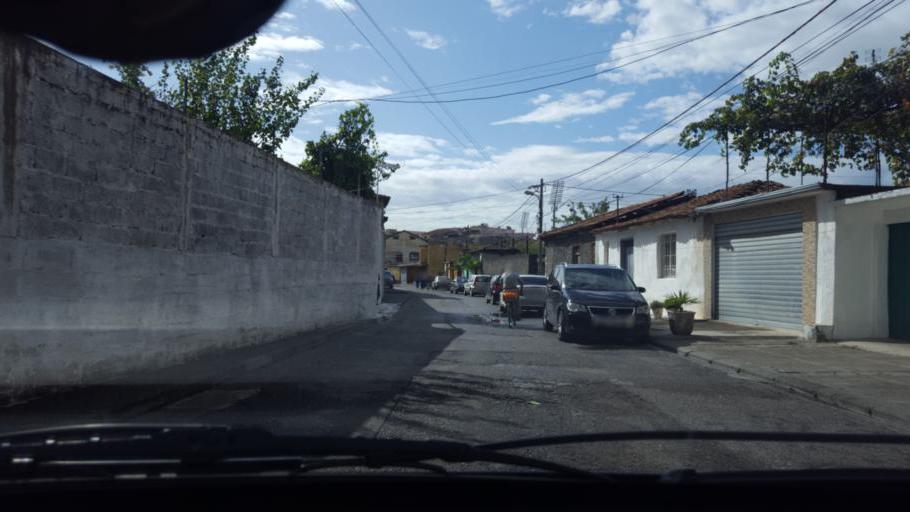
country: AL
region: Shkoder
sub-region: Rrethi i Shkodres
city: Shkoder
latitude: 42.0736
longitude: 19.5077
